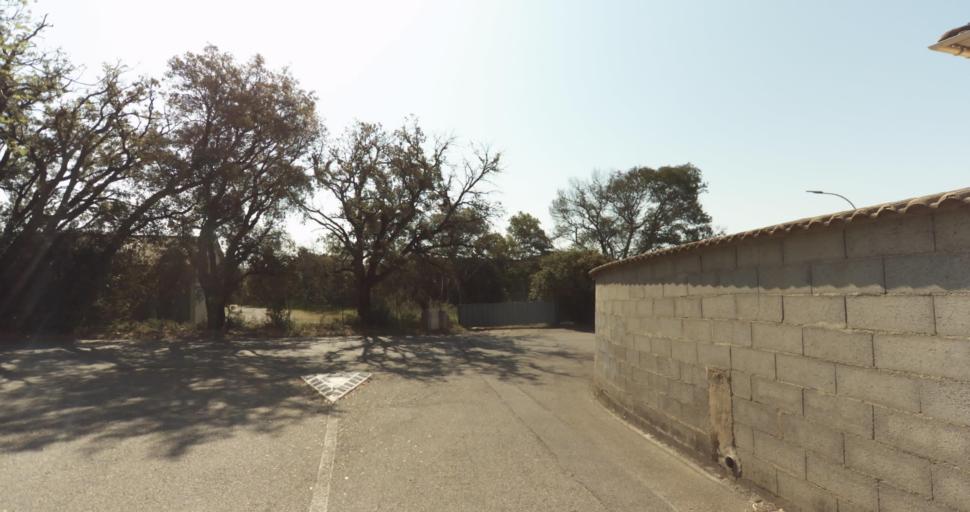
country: FR
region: Corsica
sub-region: Departement de la Haute-Corse
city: Biguglia
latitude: 42.6228
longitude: 9.4354
